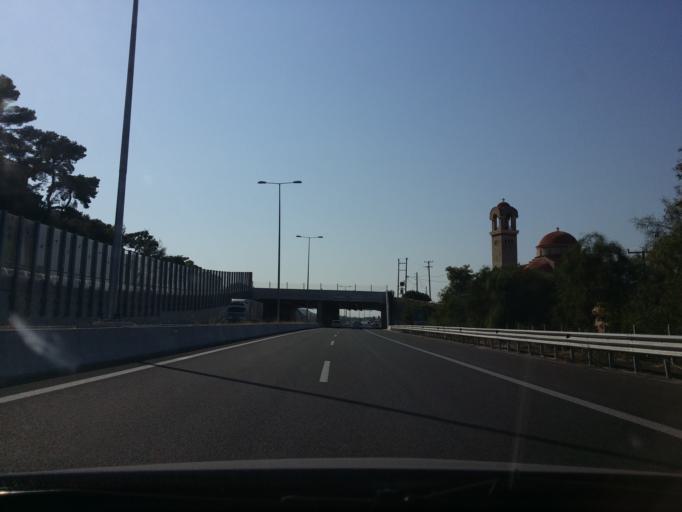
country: GR
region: Peloponnese
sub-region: Nomos Korinthias
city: Kato Dhiminio
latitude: 38.0490
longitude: 22.6858
